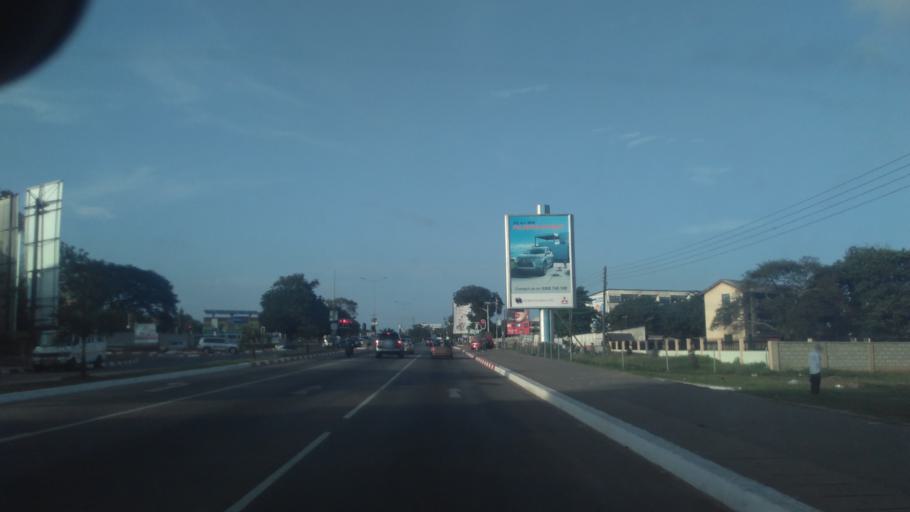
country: GH
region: Greater Accra
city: Accra
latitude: 5.5749
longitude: -0.1887
